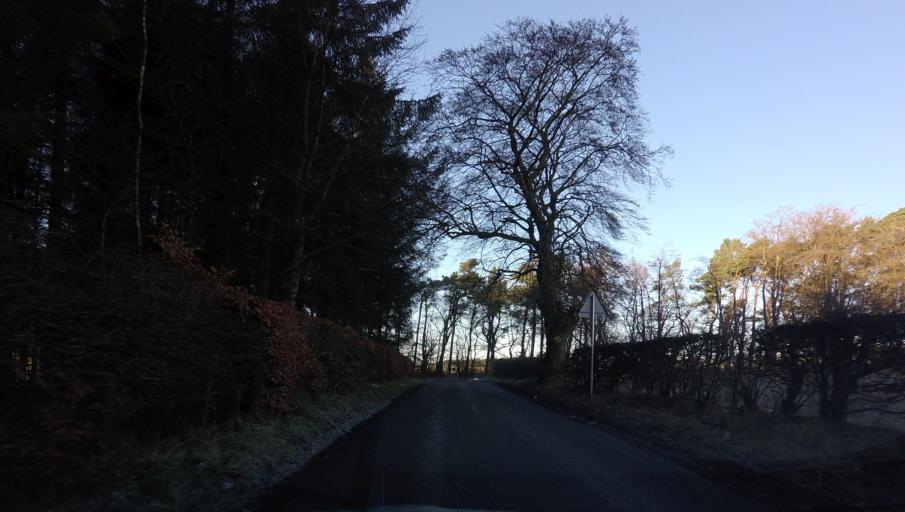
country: GB
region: Scotland
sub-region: North Lanarkshire
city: Newmains
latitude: 55.8077
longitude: -3.8609
